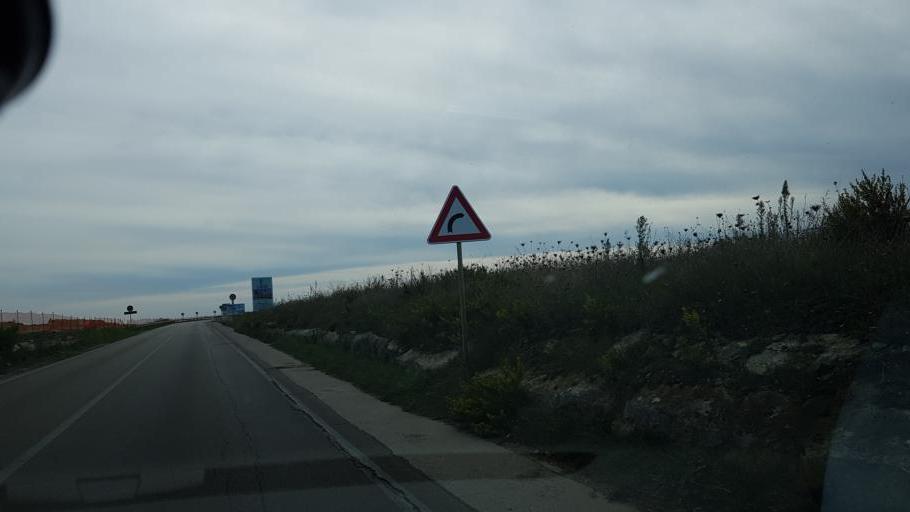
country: IT
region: Apulia
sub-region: Provincia di Lecce
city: Borgagne
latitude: 40.2844
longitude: 18.4285
